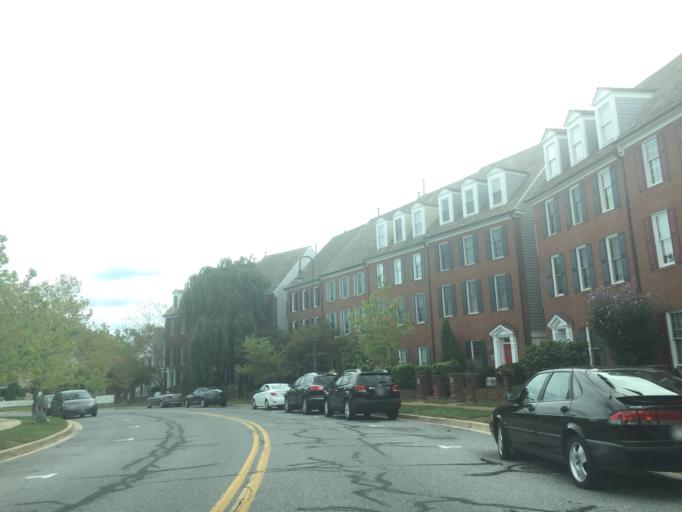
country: US
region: Maryland
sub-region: Montgomery County
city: North Potomac
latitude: 39.1230
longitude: -77.2447
